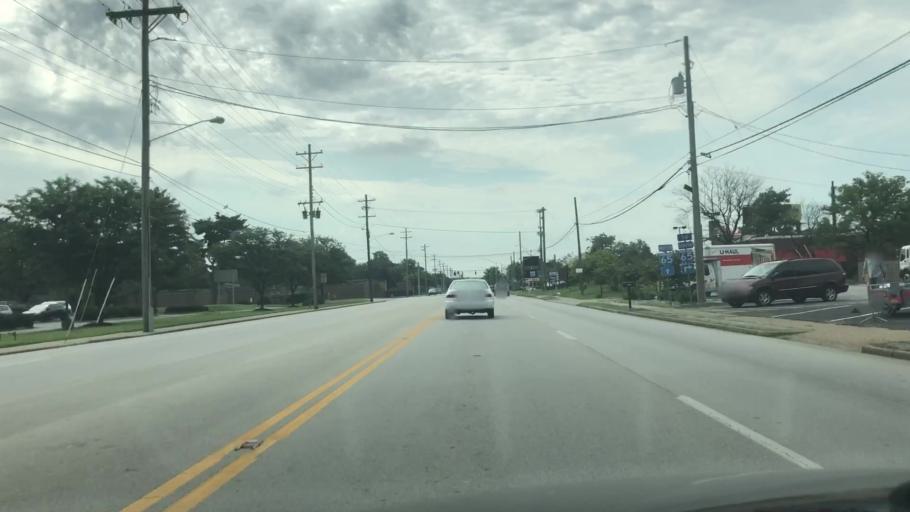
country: US
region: Kentucky
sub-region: Jefferson County
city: Audubon Park
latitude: 38.1817
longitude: -85.7202
